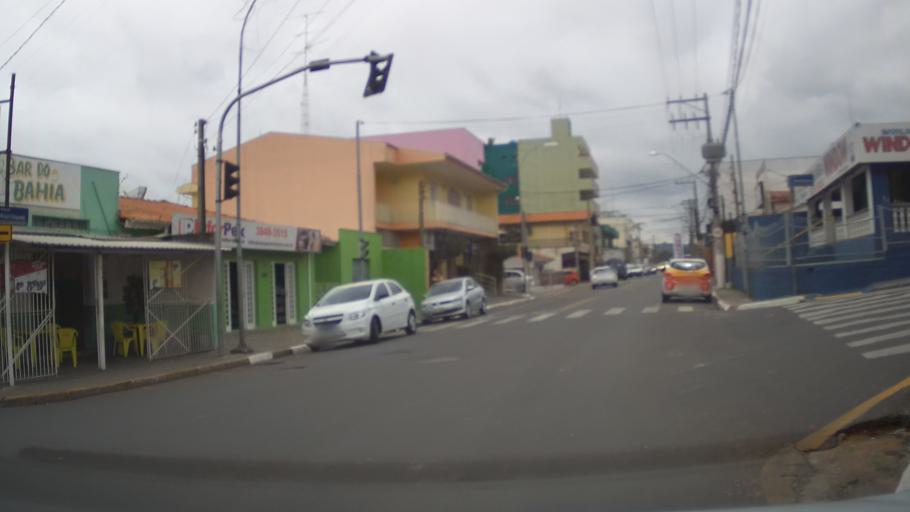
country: BR
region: Sao Paulo
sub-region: Louveira
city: Louveira
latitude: -23.0859
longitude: -46.9799
